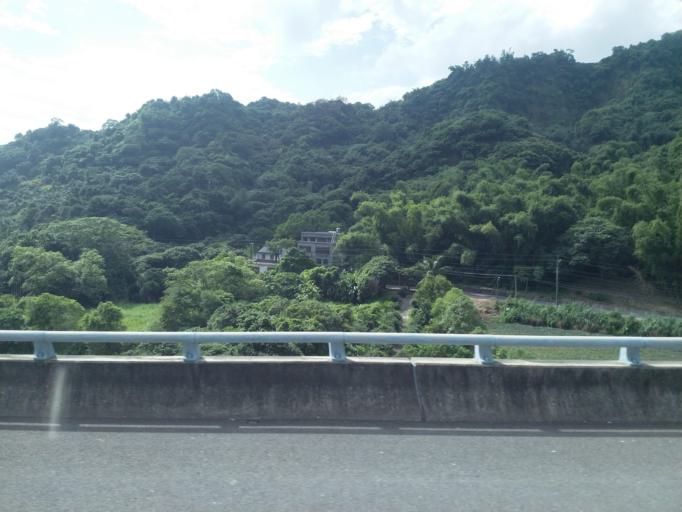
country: TW
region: Taiwan
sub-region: Pingtung
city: Pingtung
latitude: 22.7968
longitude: 120.4427
